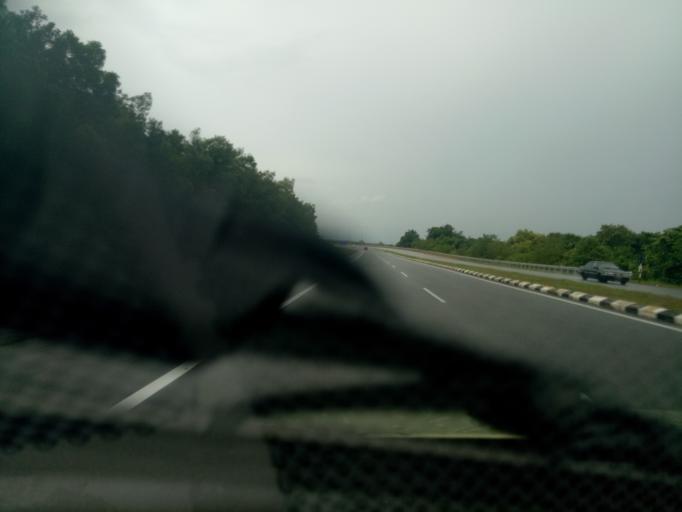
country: MY
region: Kedah
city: Sungai Petani
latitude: 5.6131
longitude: 100.5627
